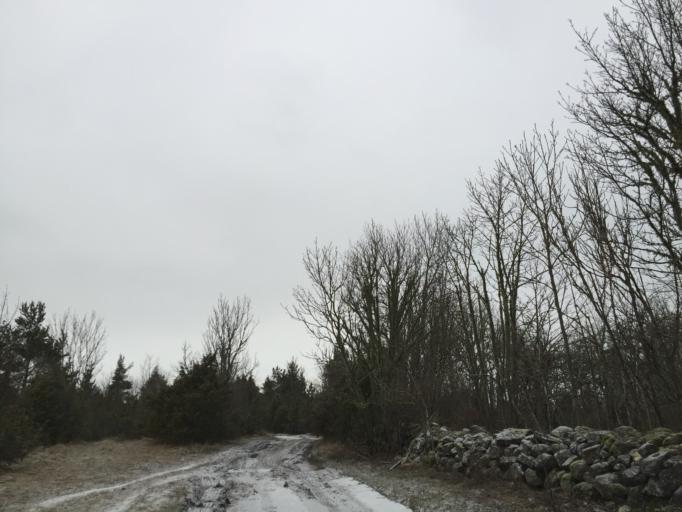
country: EE
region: Saare
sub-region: Orissaare vald
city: Orissaare
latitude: 58.6044
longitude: 23.1146
